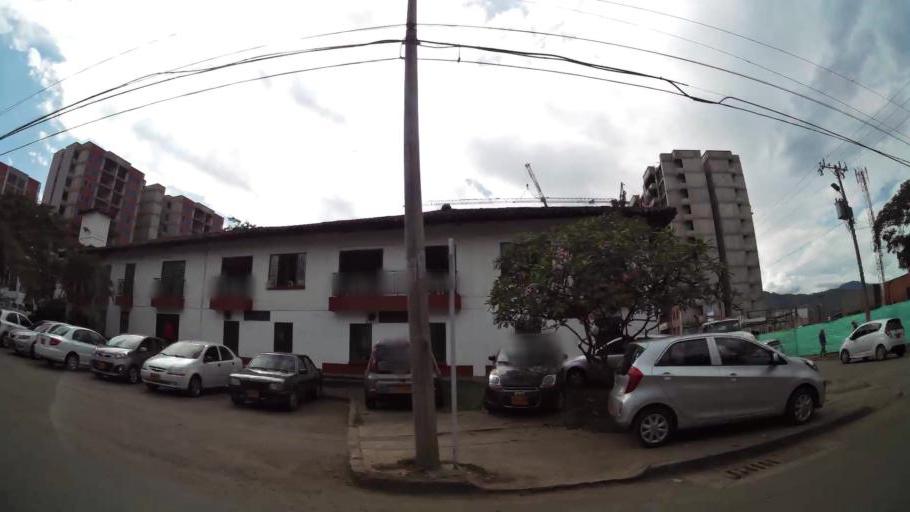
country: CO
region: Valle del Cauca
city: Cali
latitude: 3.4678
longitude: -76.5188
